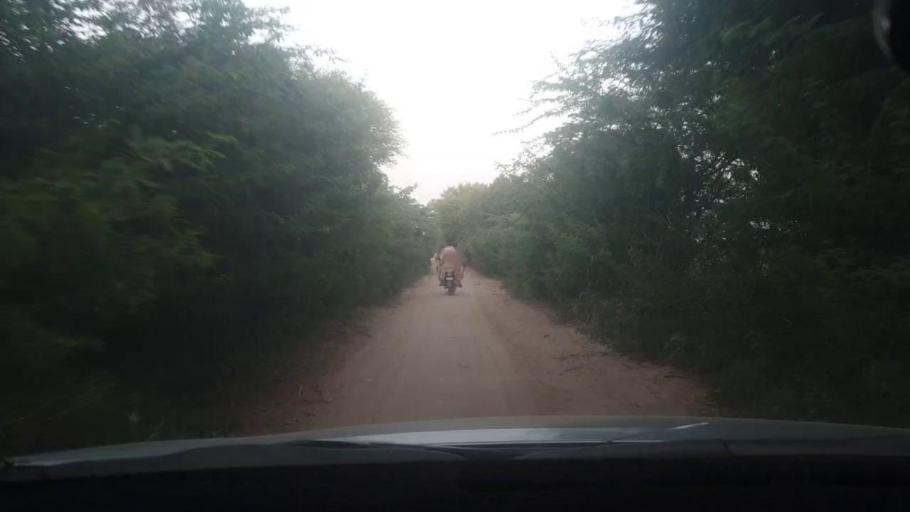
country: PK
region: Sindh
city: Pithoro
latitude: 25.7350
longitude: 69.4805
